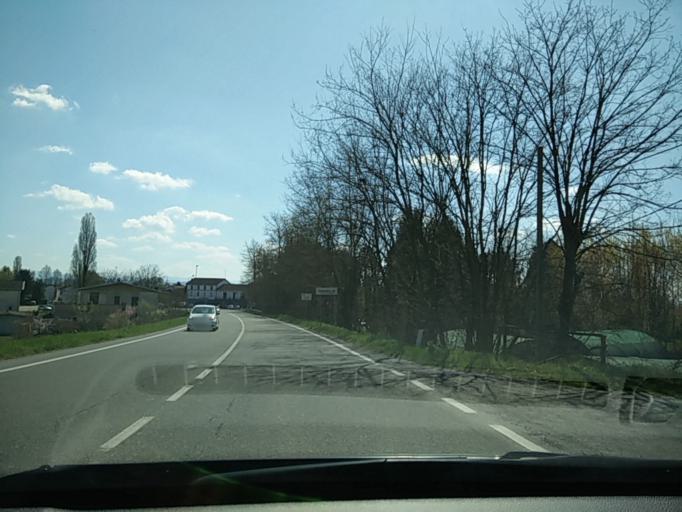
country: IT
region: Lombardy
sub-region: Provincia di Pavia
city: Mezzanino
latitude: 45.1335
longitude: 9.2237
